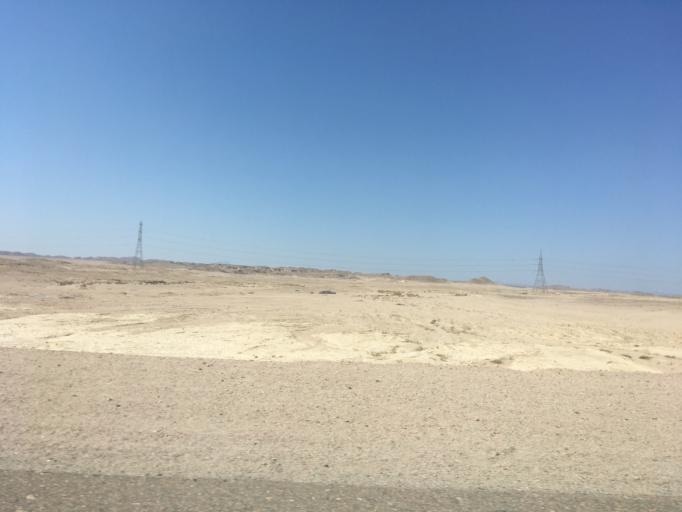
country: EG
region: Red Sea
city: Marsa Alam
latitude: 24.8781
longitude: 34.9731
